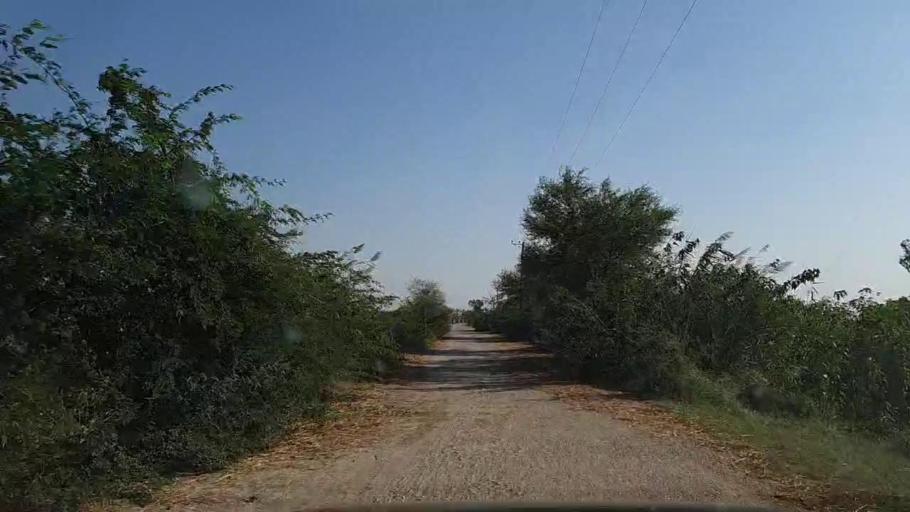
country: PK
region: Sindh
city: Thatta
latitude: 24.6348
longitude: 68.0764
